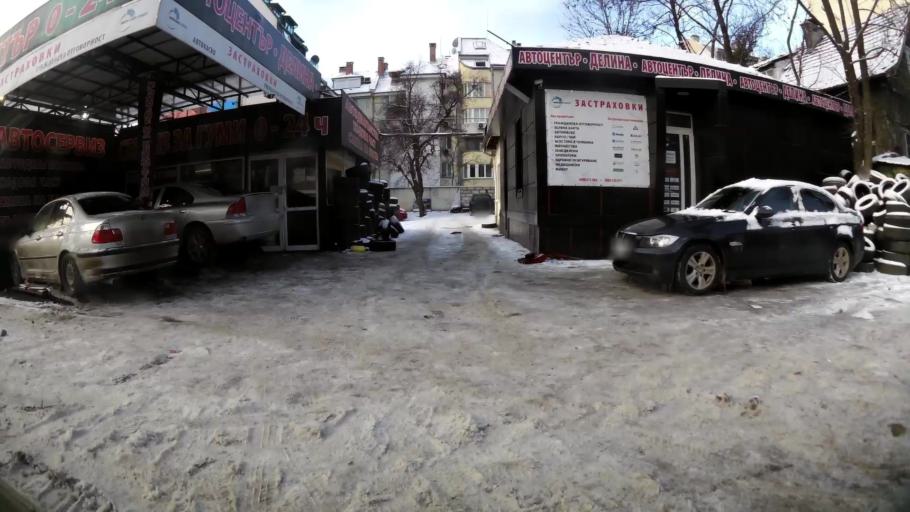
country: BG
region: Sofia-Capital
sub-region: Stolichna Obshtina
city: Sofia
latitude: 42.6729
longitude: 23.3357
